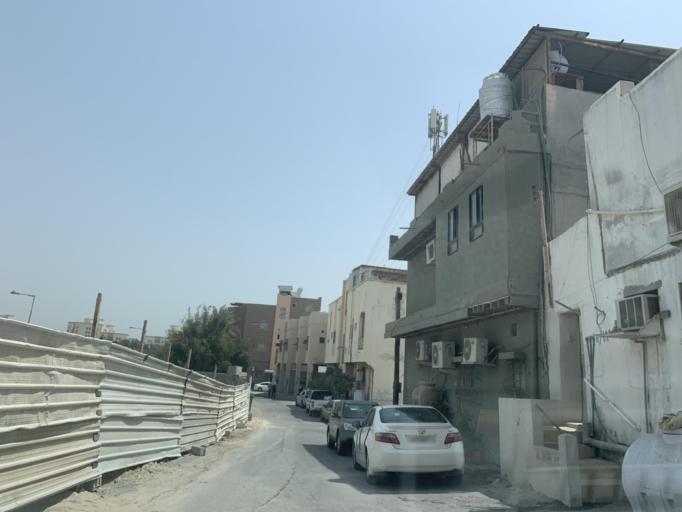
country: BH
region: Northern
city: Madinat `Isa
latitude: 26.1829
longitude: 50.5543
